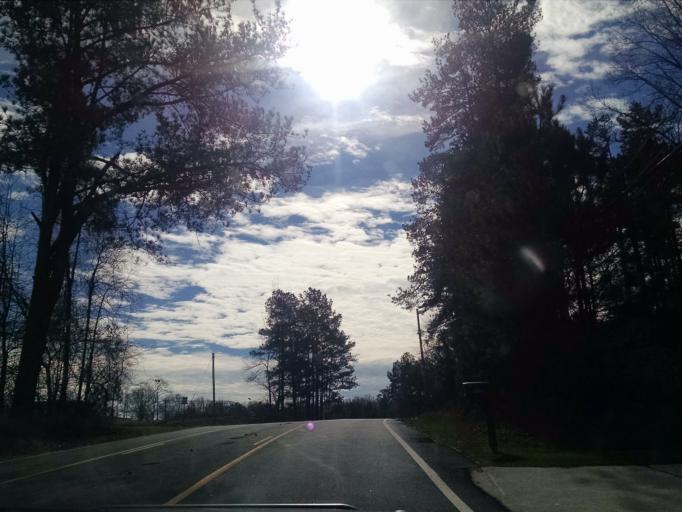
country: US
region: Georgia
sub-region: Gwinnett County
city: Sugar Hill
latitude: 34.1268
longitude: -84.0461
